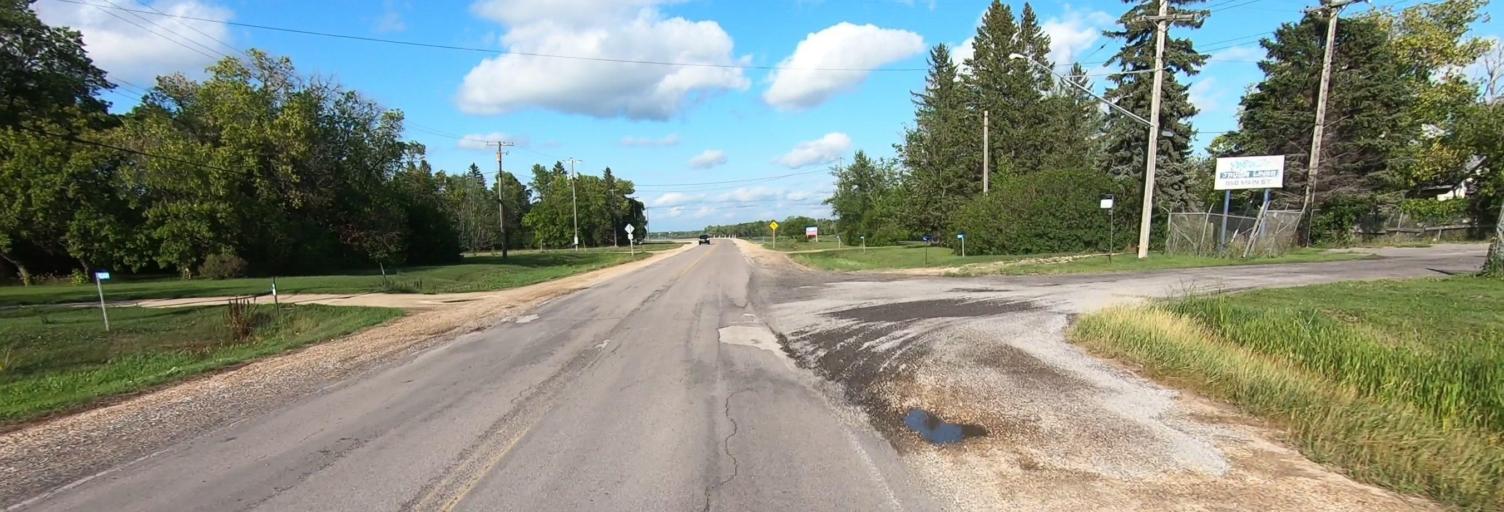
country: CA
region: Manitoba
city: Selkirk
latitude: 50.1670
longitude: -96.8665
